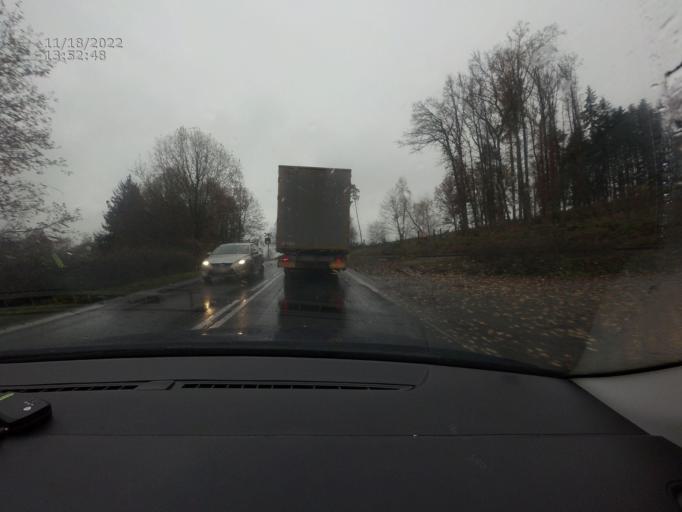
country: CZ
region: Jihocesky
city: Sedlice
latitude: 49.3943
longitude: 13.9159
